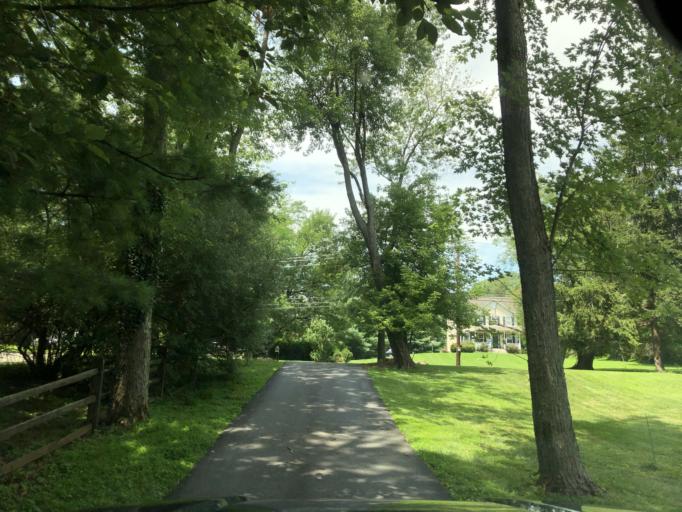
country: US
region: Maryland
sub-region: Baltimore County
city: Garrison
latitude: 39.4590
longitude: -76.7239
